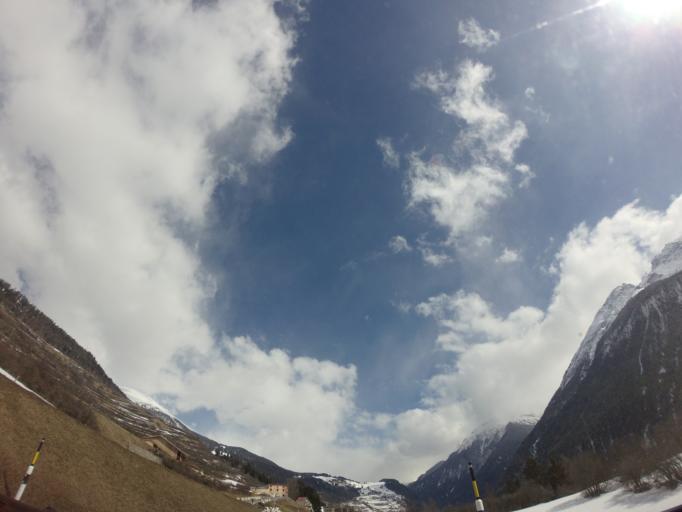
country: CH
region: Grisons
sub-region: Inn District
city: Scuol
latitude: 46.8176
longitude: 10.3553
